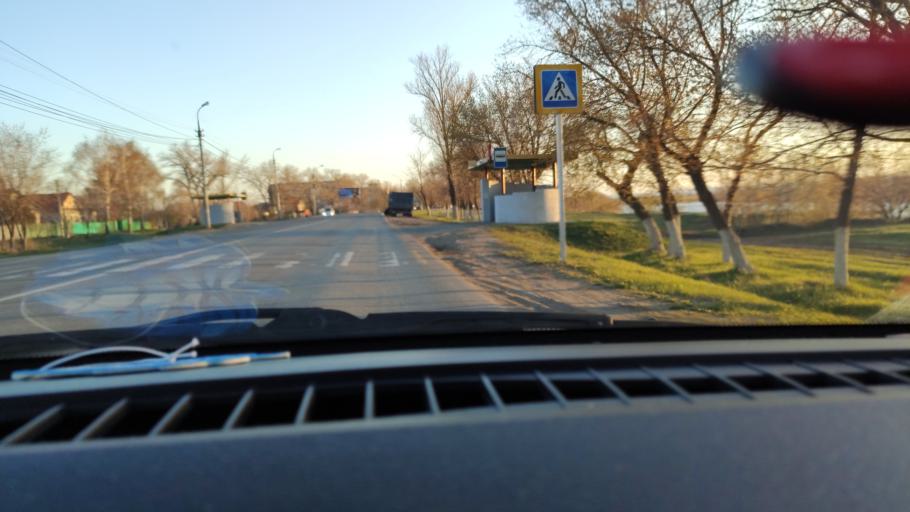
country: RU
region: Saratov
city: Engel's
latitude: 51.4485
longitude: 46.0792
